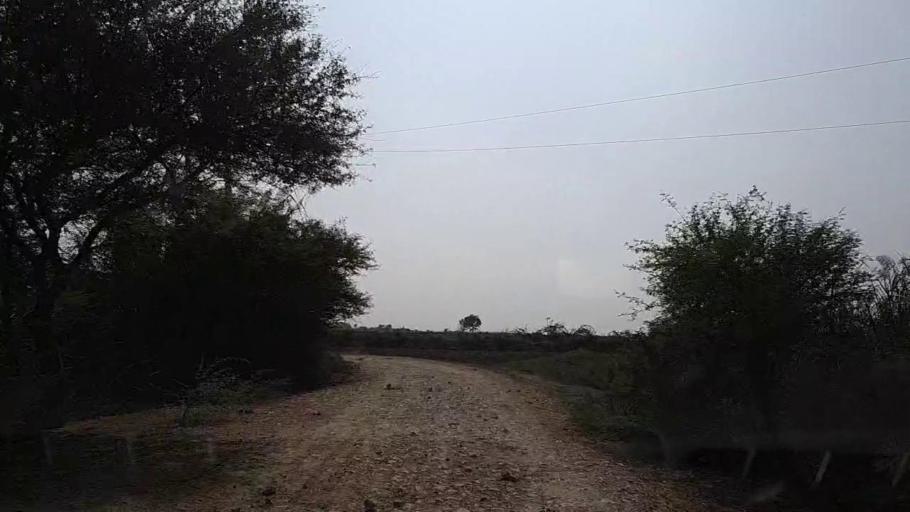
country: PK
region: Sindh
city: Mirpur Sakro
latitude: 24.5283
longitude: 67.8011
